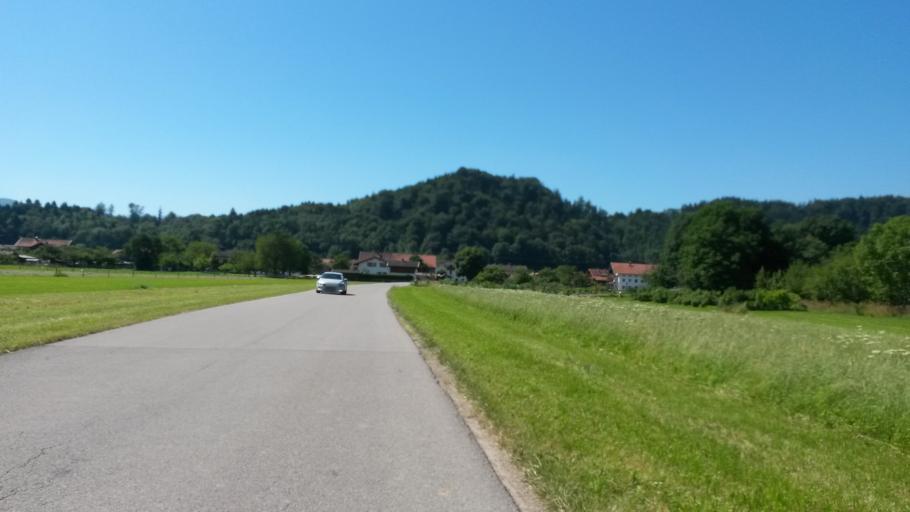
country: DE
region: Bavaria
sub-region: Upper Bavaria
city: Marquartstein
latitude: 47.7659
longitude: 12.4525
